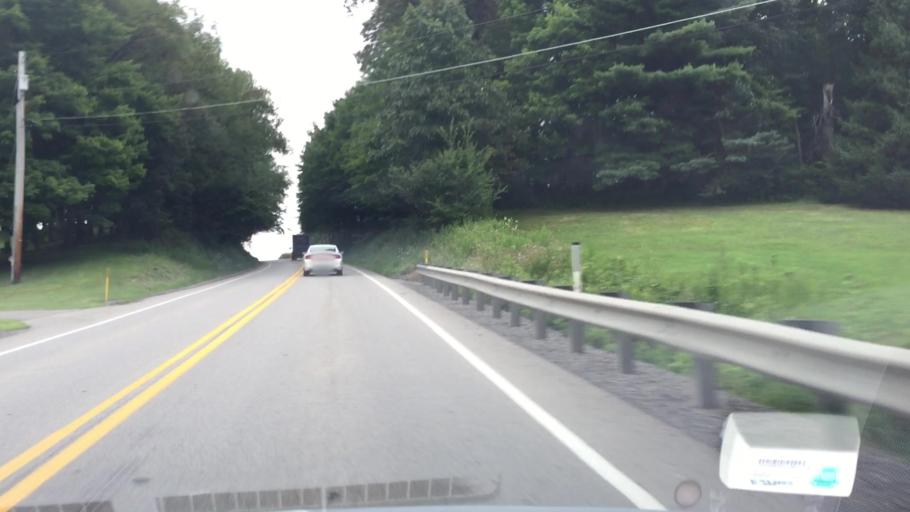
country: US
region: Pennsylvania
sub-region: Butler County
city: Nixon
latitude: 40.7242
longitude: -79.9152
